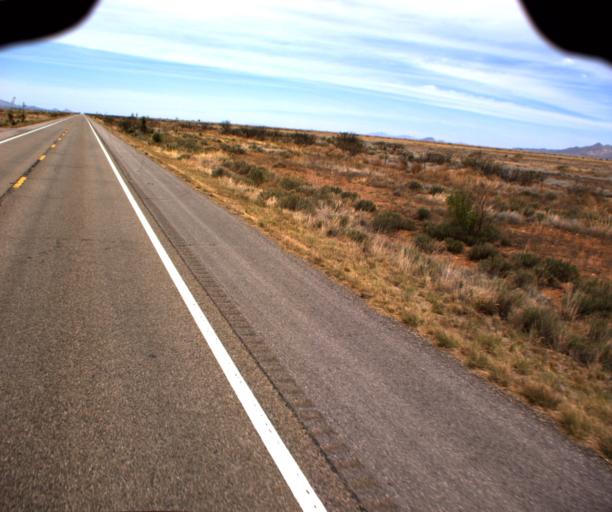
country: US
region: Arizona
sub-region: Cochise County
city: Pirtleville
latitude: 31.5174
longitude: -109.6443
